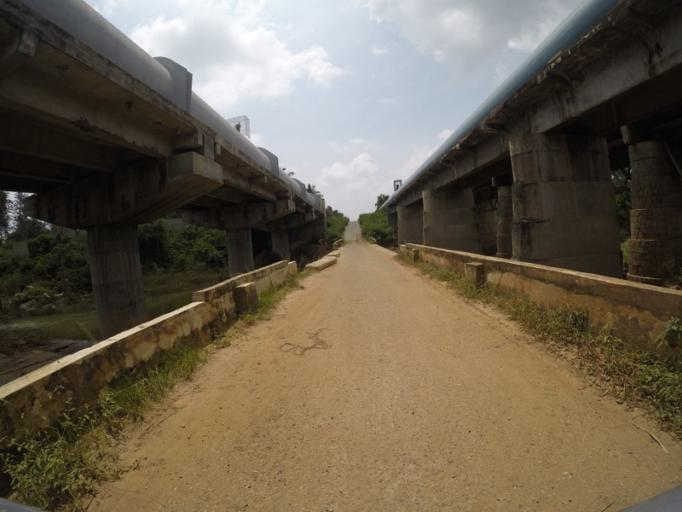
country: IN
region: Karnataka
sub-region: Ramanagara
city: Kanakapura
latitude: 12.7363
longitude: 77.4853
